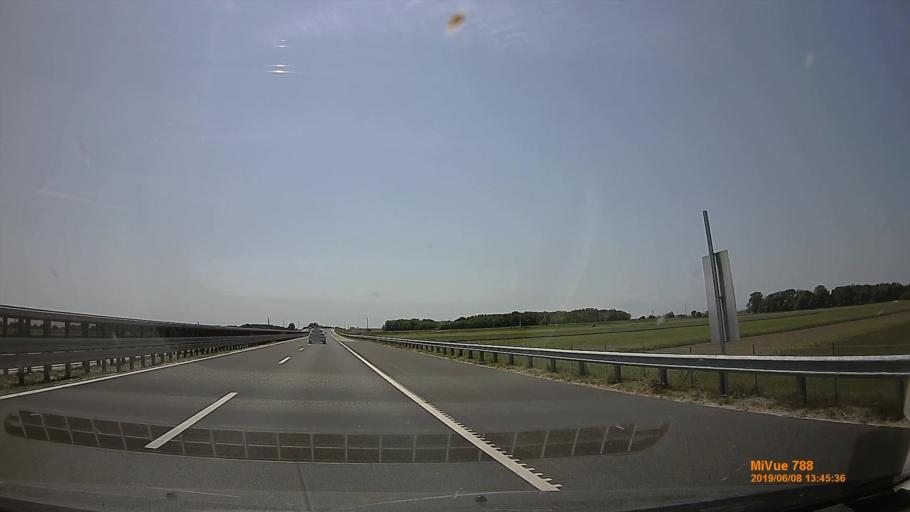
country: HU
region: Gyor-Moson-Sopron
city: Beled
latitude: 47.4291
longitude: 17.0714
